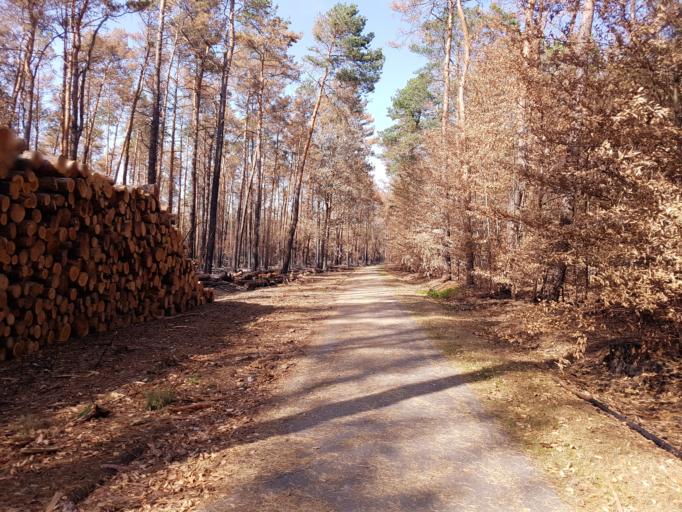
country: DE
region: Brandenburg
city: Finsterwalde
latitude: 51.6282
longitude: 13.6714
